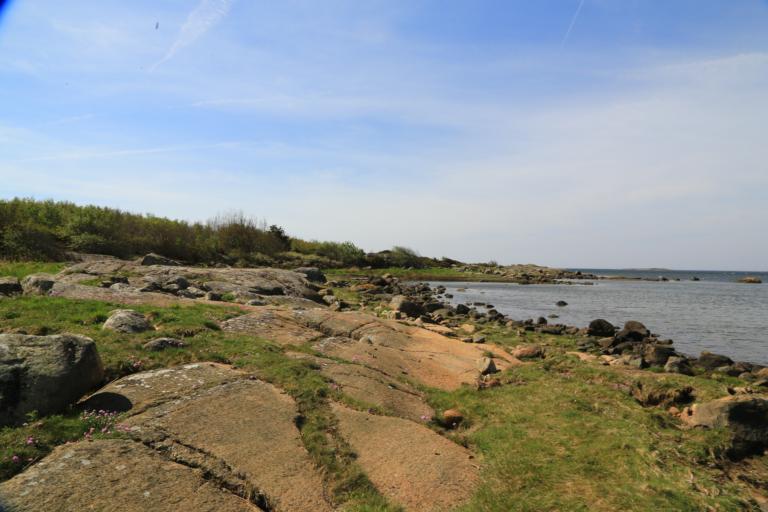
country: SE
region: Halland
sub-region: Varbergs Kommun
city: Varberg
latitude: 57.1355
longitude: 12.2174
